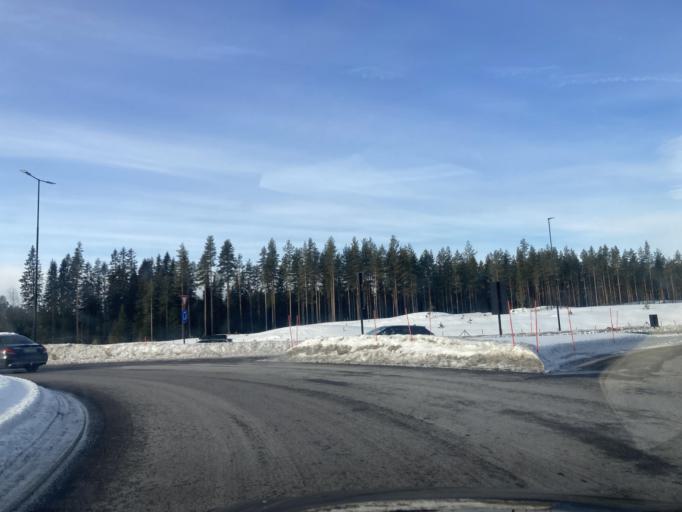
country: NO
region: Hedmark
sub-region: Elverum
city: Elverum
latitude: 60.8879
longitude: 11.5084
